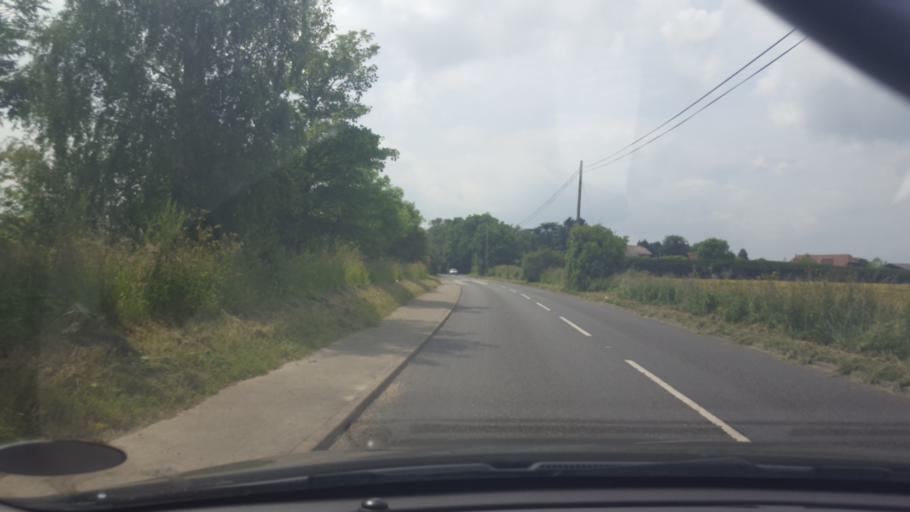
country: GB
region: England
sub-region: Essex
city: Great Bentley
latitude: 51.8779
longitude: 1.1135
